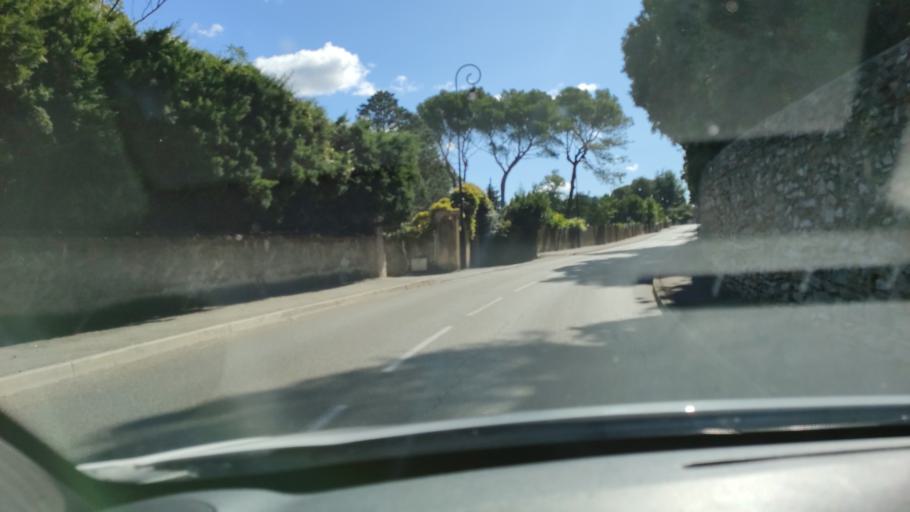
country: FR
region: Languedoc-Roussillon
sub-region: Departement du Gard
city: Villeneuve-les-Avignon
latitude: 43.9652
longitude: 4.7845
